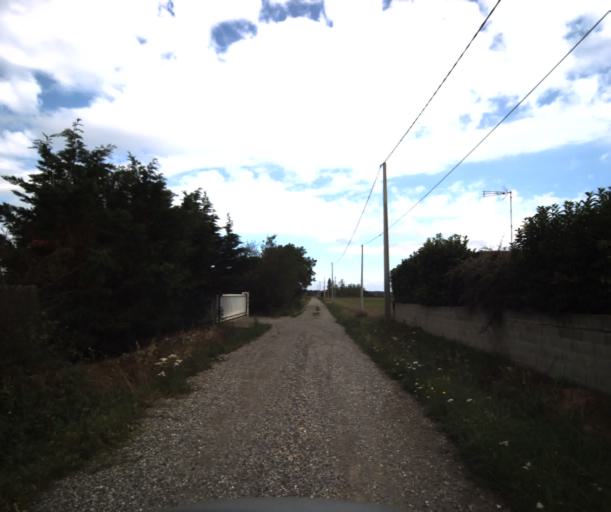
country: FR
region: Midi-Pyrenees
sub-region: Departement de la Haute-Garonne
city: Lacasse
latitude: 43.3919
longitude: 1.2315
